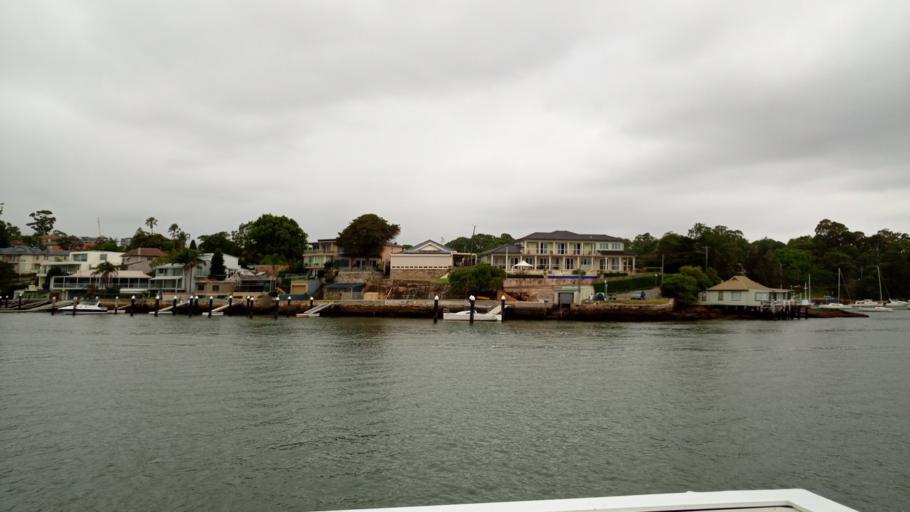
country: AU
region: New South Wales
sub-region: Hunters Hill
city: Gladesville
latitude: -33.8423
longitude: 151.1239
